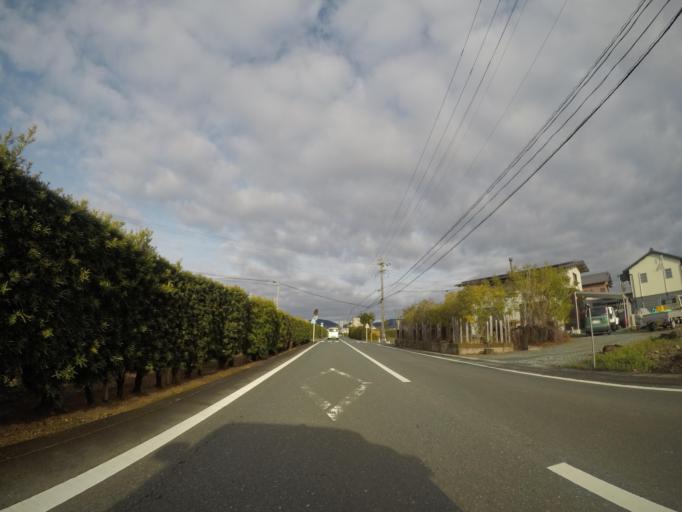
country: JP
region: Shizuoka
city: Hamakita
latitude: 34.8222
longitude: 137.7495
